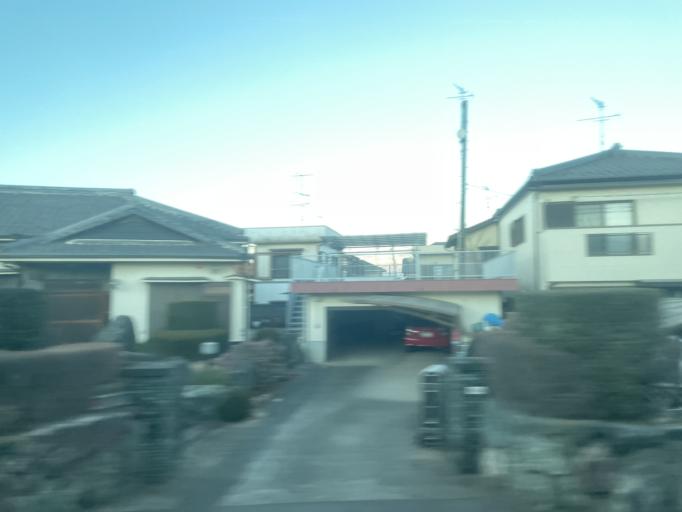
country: JP
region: Saitama
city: Fukayacho
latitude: 36.1957
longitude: 139.2607
